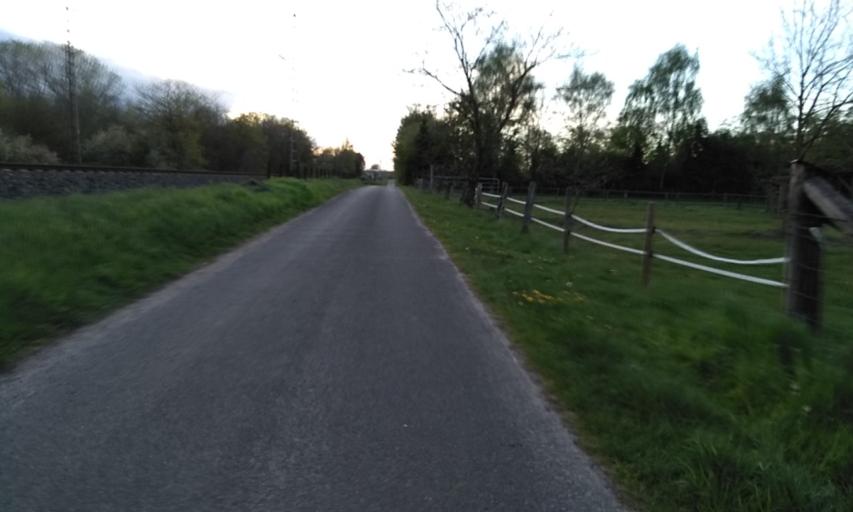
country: DE
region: Lower Saxony
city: Nottensdorf
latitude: 53.4952
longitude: 9.6052
